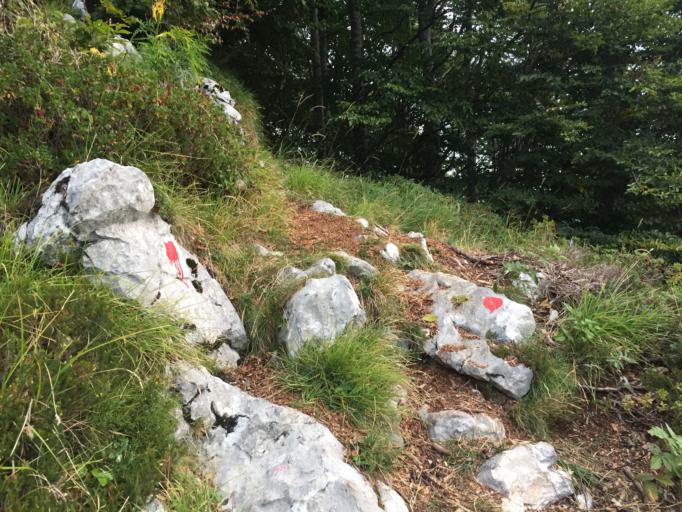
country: IT
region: Friuli Venezia Giulia
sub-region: Provincia di Pordenone
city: Budoia
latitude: 46.1105
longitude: 12.5110
